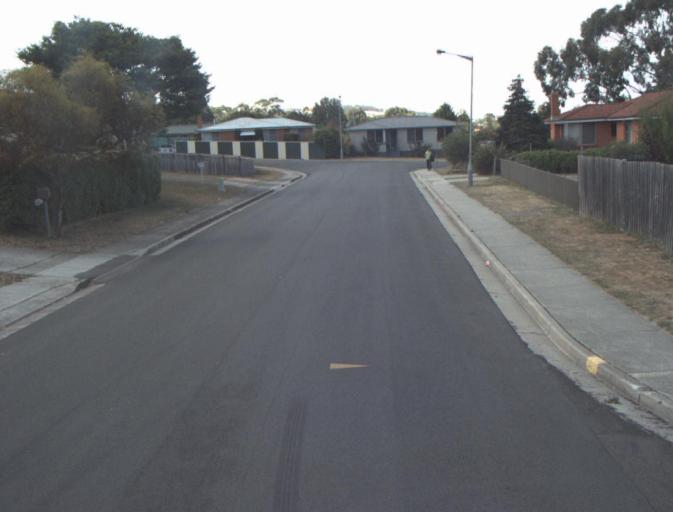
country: AU
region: Tasmania
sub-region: Launceston
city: Newstead
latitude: -41.4133
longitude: 147.1742
